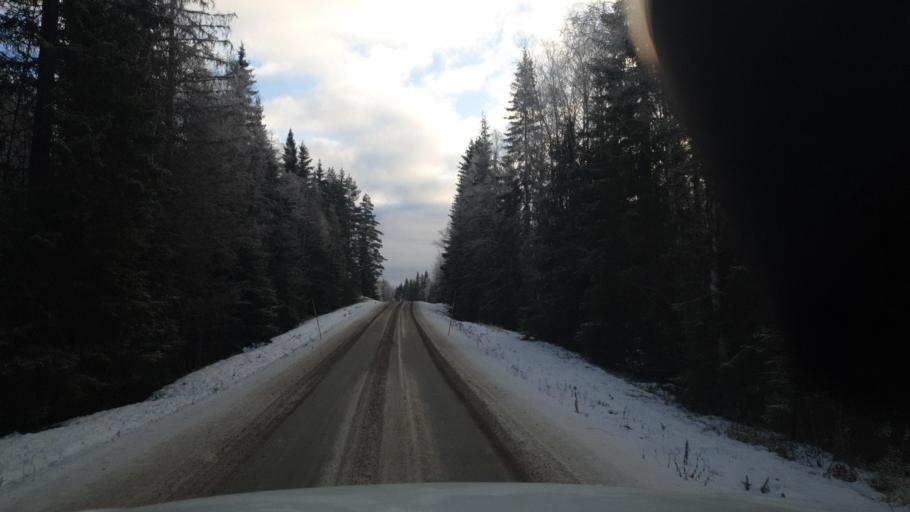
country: SE
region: Vaermland
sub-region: Eda Kommun
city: Charlottenberg
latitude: 60.0534
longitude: 12.5628
